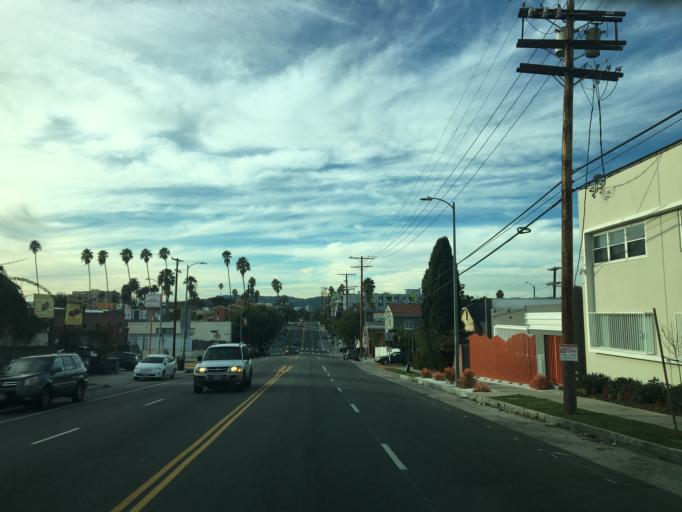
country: US
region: California
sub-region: Los Angeles County
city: Silver Lake
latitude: 34.0743
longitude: -118.2787
